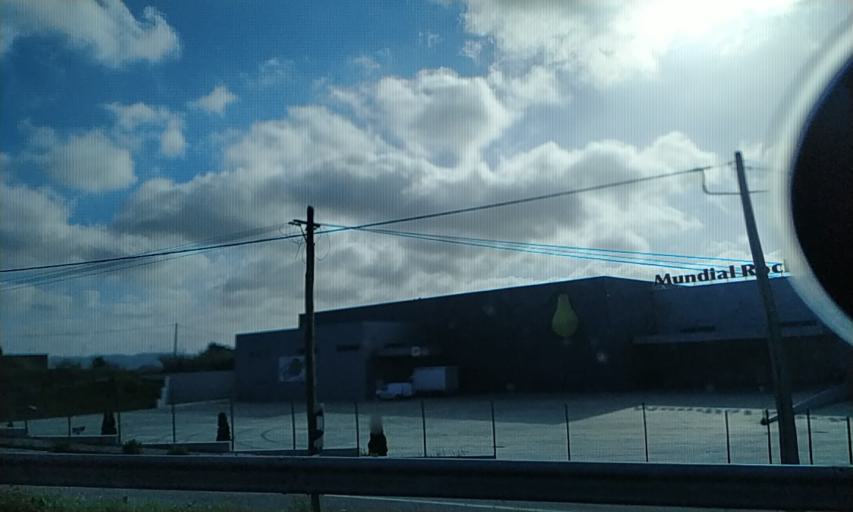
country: PT
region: Leiria
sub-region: Obidos
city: Obidos
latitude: 39.3342
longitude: -9.1743
